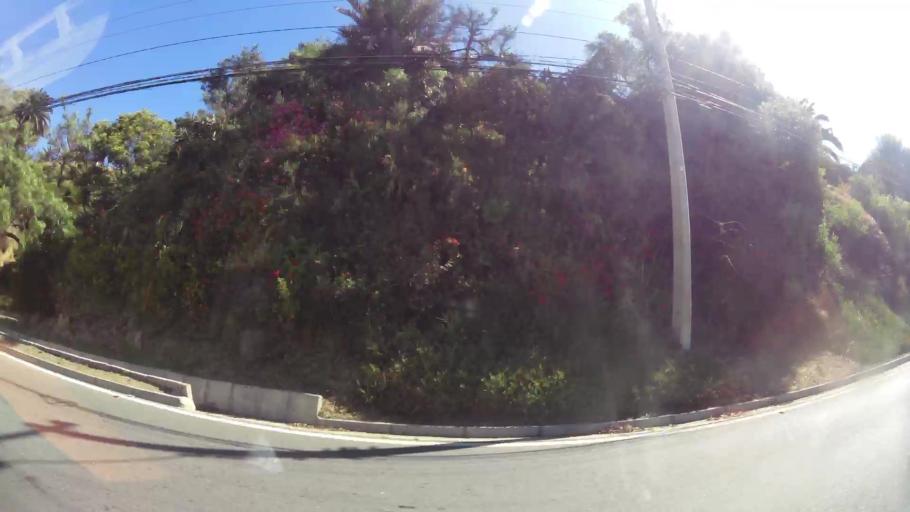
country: CL
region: Valparaiso
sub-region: Provincia de Valparaiso
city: Valparaiso
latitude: -33.0232
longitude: -71.6440
